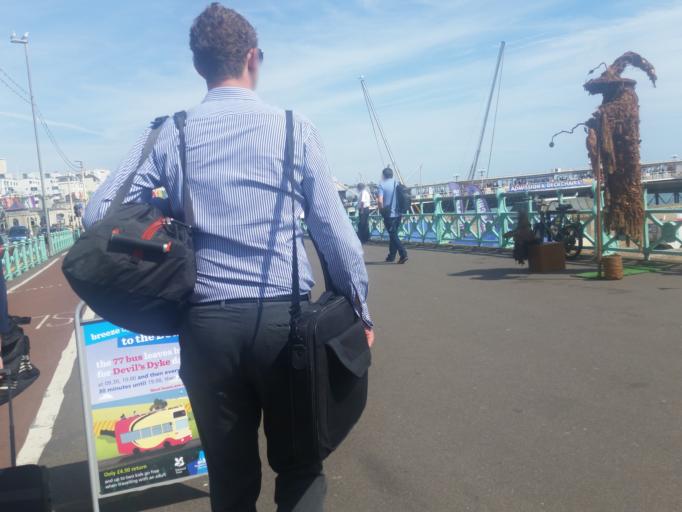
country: GB
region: England
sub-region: Brighton and Hove
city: Brighton
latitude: 50.8193
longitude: -0.1380
